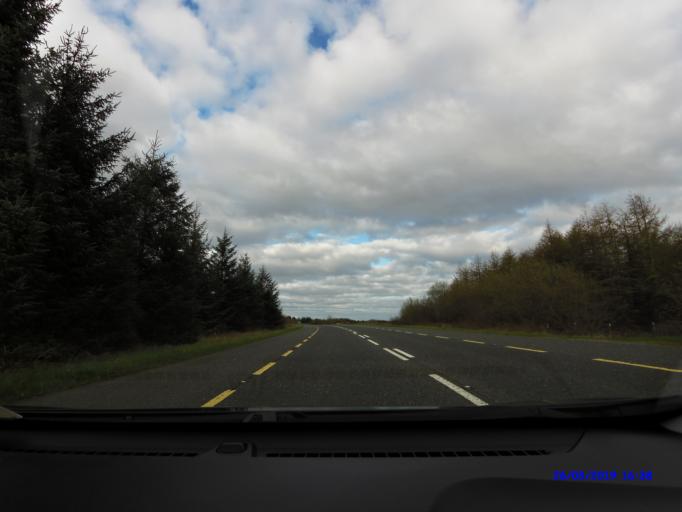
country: IE
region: Connaught
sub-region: Maigh Eo
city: Ballyhaunis
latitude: 53.8828
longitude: -8.8095
